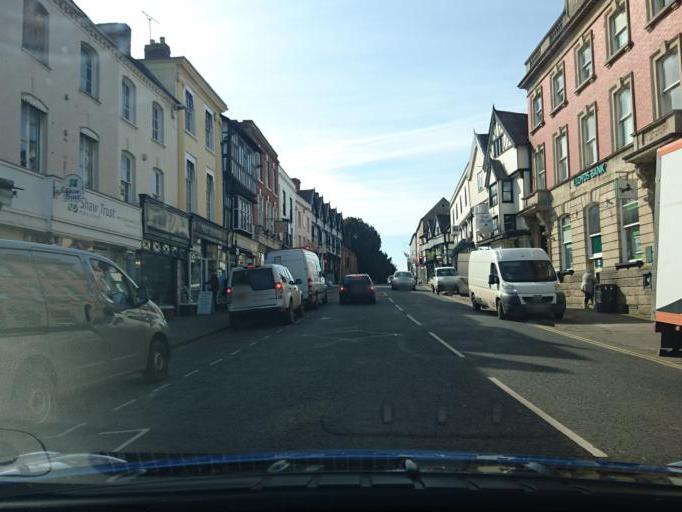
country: GB
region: England
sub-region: Herefordshire
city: Ledbury
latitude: 52.0364
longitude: -2.4225
